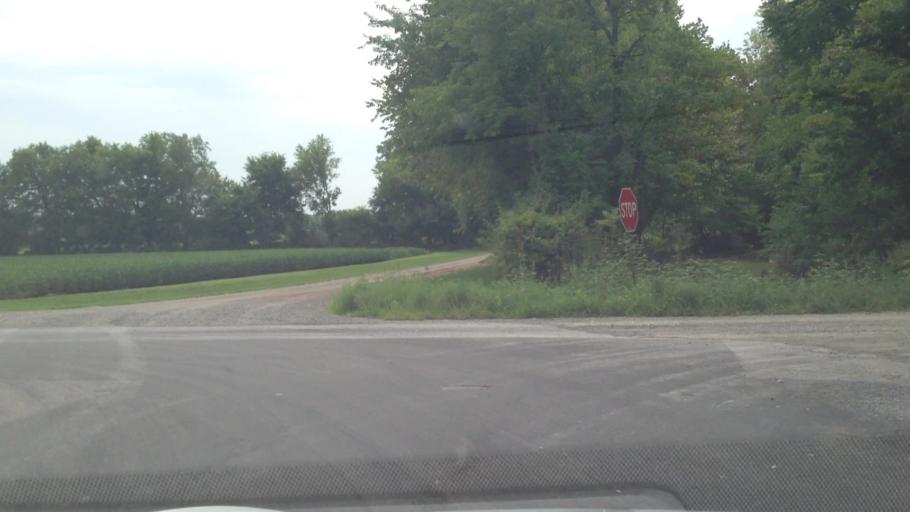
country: US
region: Kansas
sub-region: Crawford County
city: Girard
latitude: 37.4995
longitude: -94.8699
